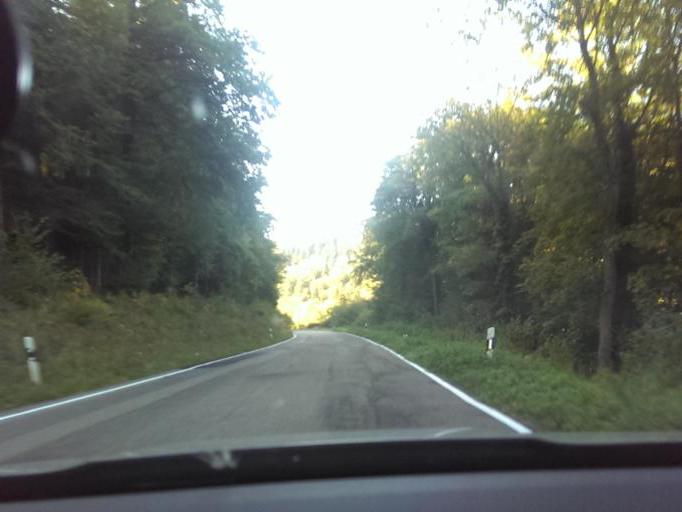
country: DE
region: Baden-Wuerttemberg
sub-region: Karlsruhe Region
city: Tiefenbronn
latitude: 48.8225
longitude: 8.7886
